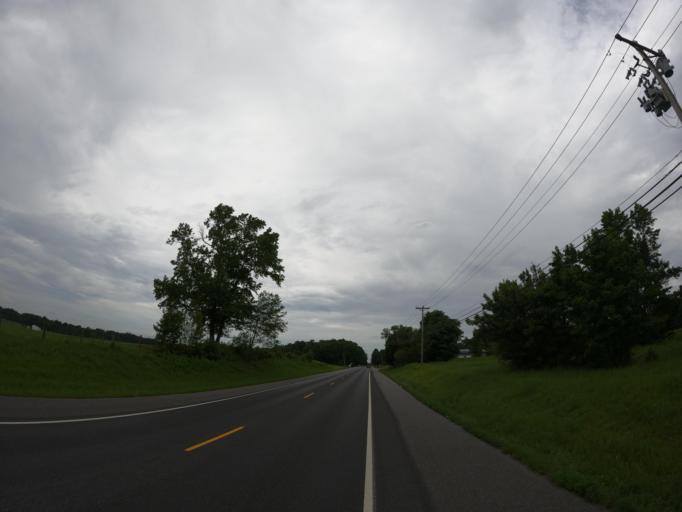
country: US
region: Maryland
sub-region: Saint Mary's County
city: Lexington Park
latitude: 38.2085
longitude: -76.5123
